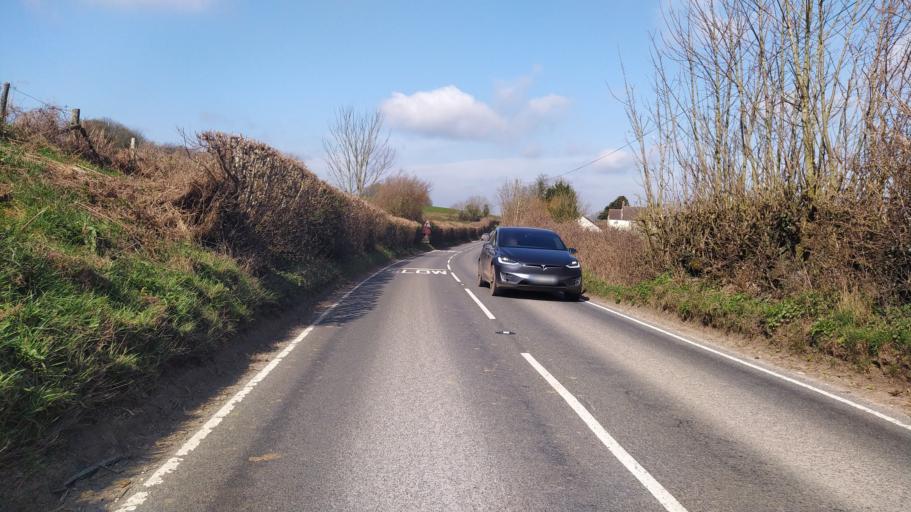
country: GB
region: England
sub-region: Somerset
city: Crewkerne
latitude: 50.8523
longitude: -2.7726
